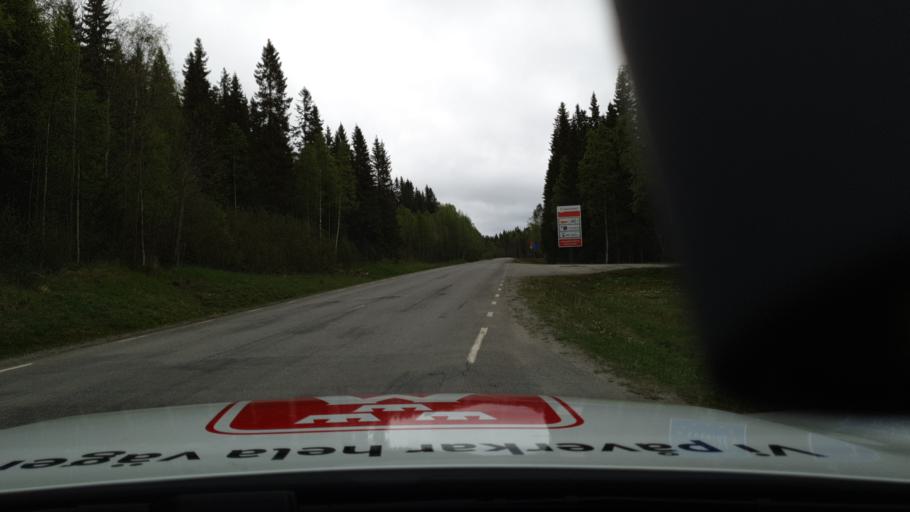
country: NO
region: Nord-Trondelag
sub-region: Lierne
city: Sandvika
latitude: 64.4777
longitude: 14.0859
